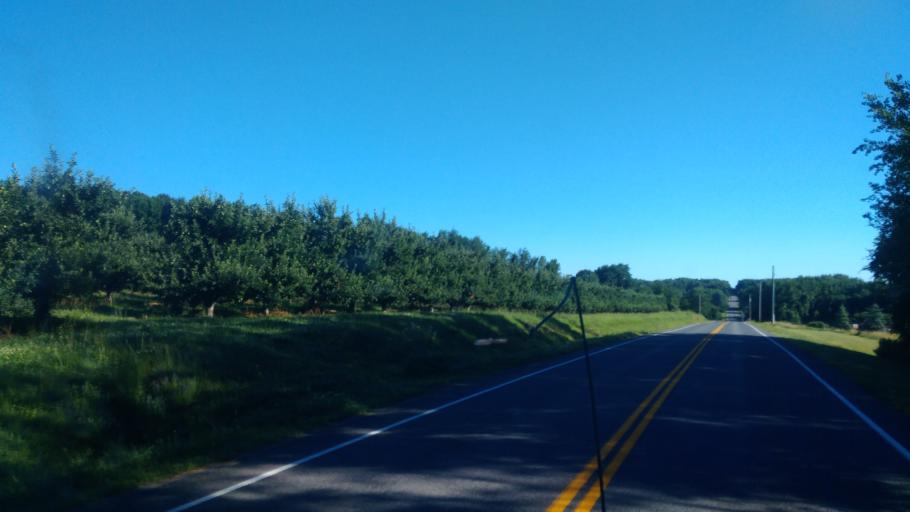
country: US
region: New York
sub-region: Wayne County
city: Sodus
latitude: 43.2098
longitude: -77.1110
